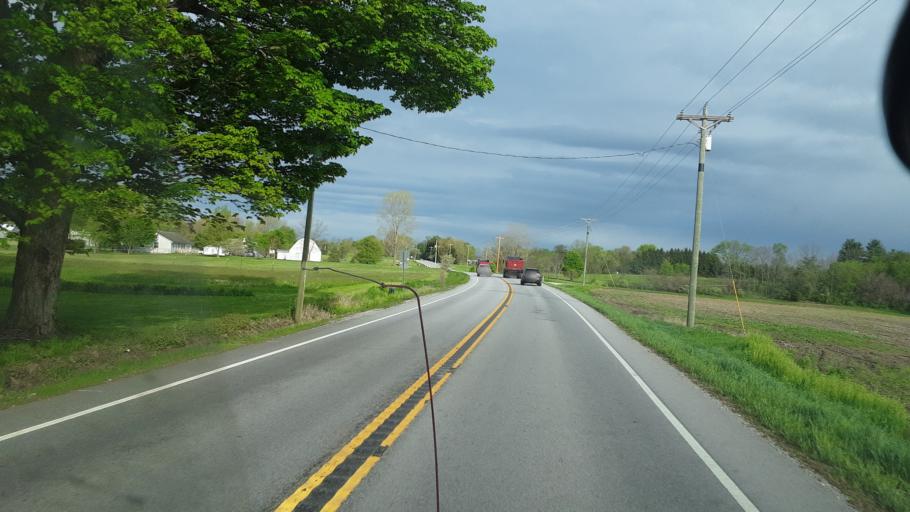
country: US
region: Indiana
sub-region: Whitley County
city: Churubusco
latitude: 41.2549
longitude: -85.3537
